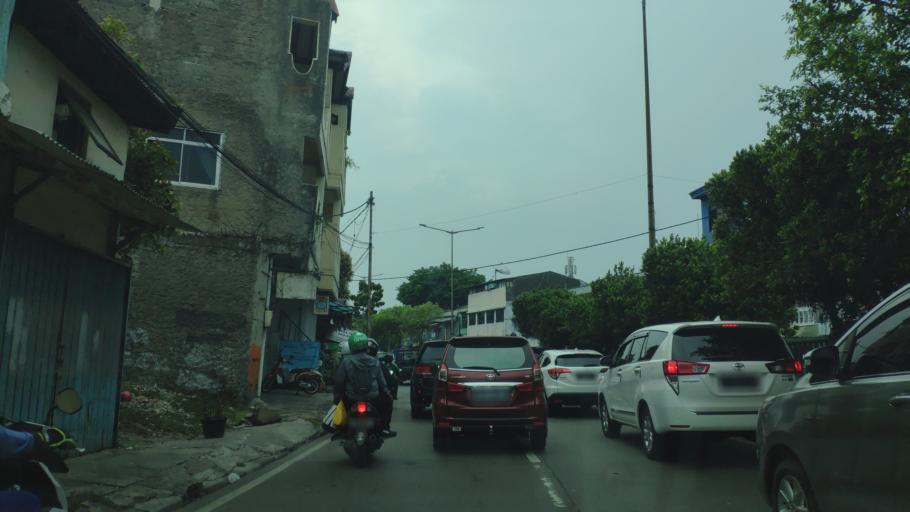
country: ID
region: Jakarta Raya
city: Jakarta
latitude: -6.1877
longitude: 106.8072
